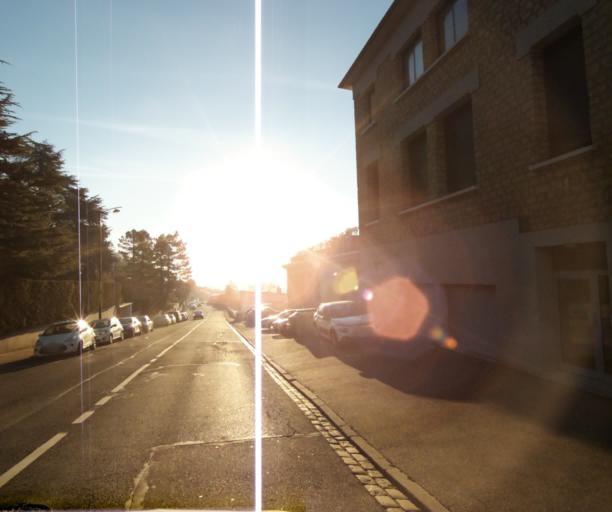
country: FR
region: Lorraine
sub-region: Departement de Meurthe-et-Moselle
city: Laxou
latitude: 48.6886
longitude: 6.1377
